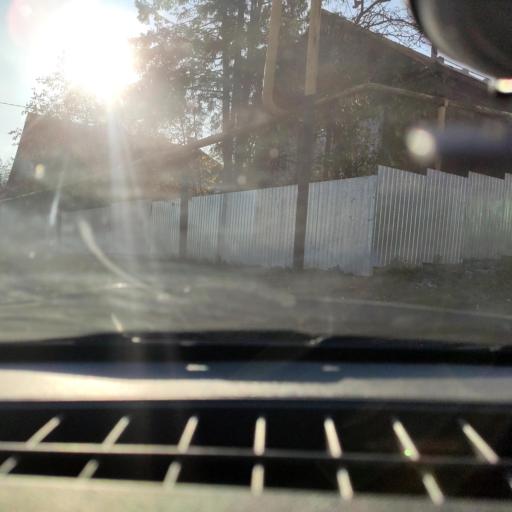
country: RU
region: Bashkortostan
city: Ufa
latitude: 54.7805
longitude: 56.0433
